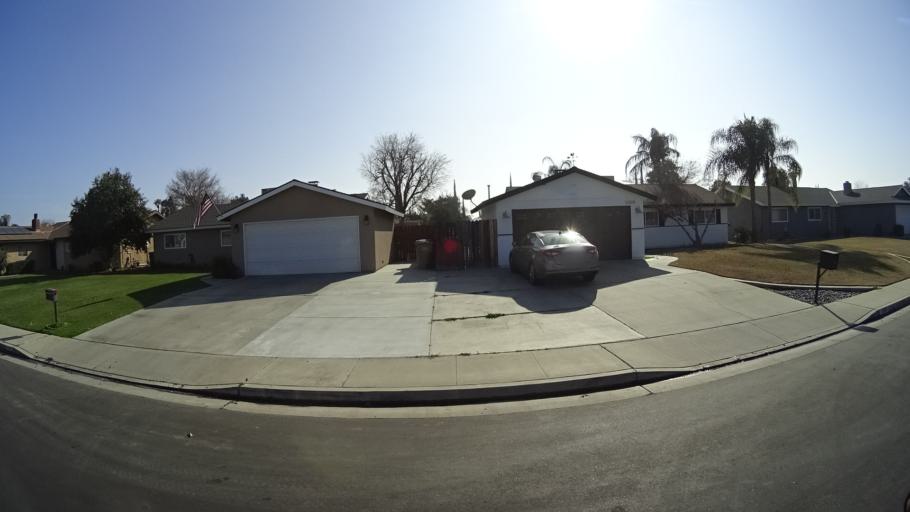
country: US
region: California
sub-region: Kern County
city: Bakersfield
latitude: 35.3291
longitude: -119.0606
